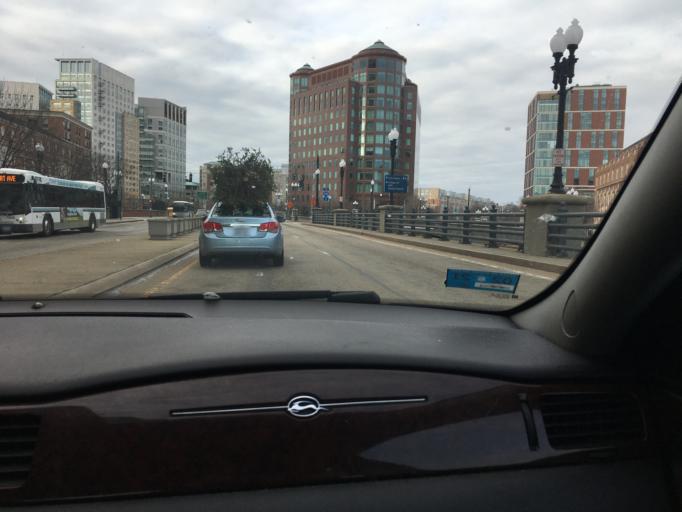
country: US
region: Rhode Island
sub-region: Providence County
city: Providence
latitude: 41.8258
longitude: -71.4093
